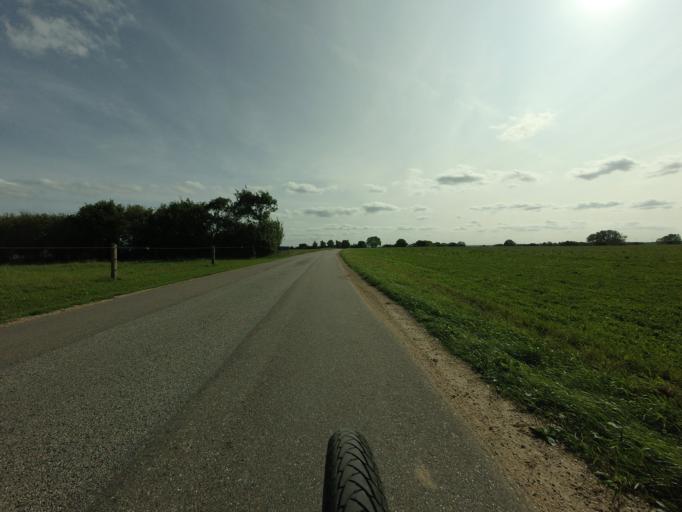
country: DK
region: Zealand
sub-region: Faxe Kommune
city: Fakse
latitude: 55.1952
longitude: 12.1092
